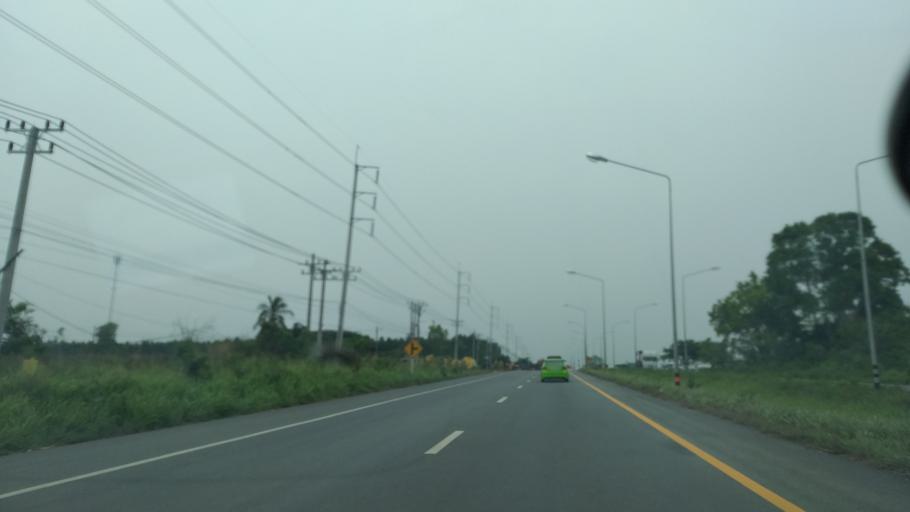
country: TH
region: Chon Buri
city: Ko Chan
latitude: 13.4584
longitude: 101.2839
